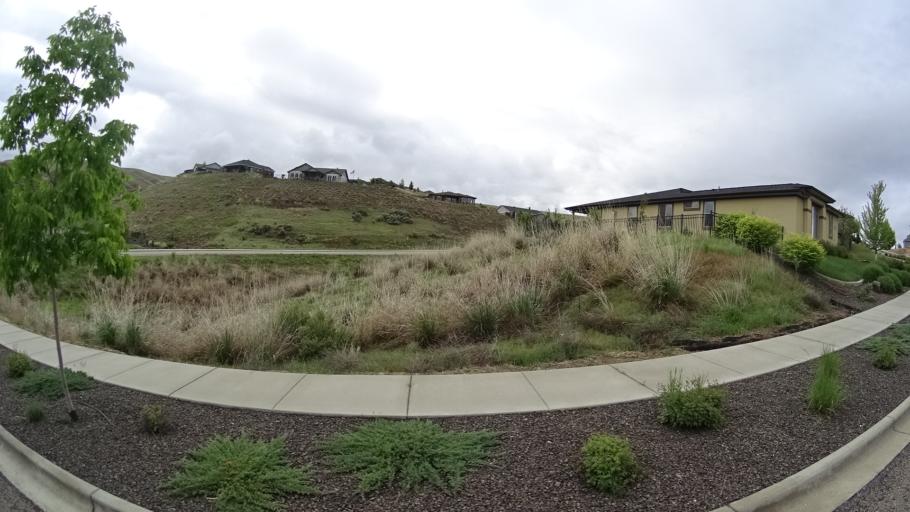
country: US
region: Idaho
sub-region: Ada County
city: Eagle
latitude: 43.7724
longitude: -116.2602
